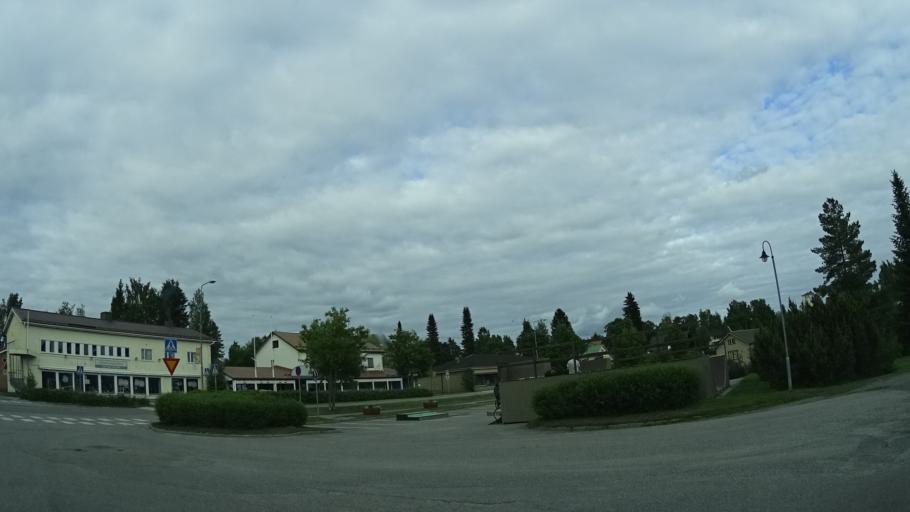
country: FI
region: Paijanne Tavastia
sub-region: Lahti
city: Sysmae
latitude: 61.5012
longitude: 25.6901
